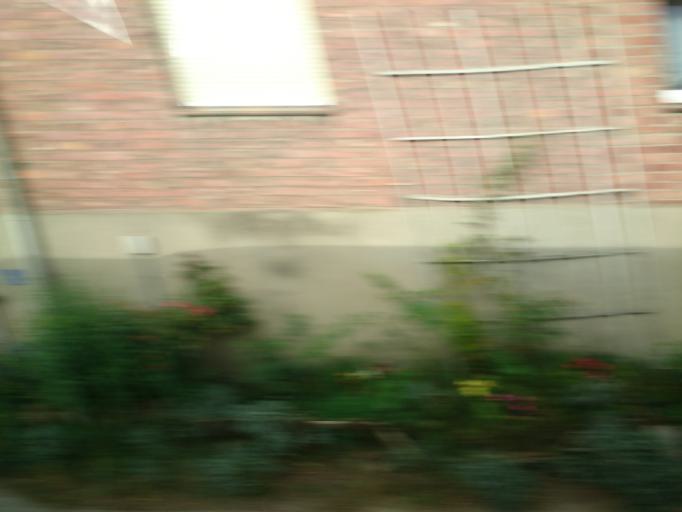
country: DE
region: Mecklenburg-Vorpommern
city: Jatznick
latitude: 53.5474
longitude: 13.9691
